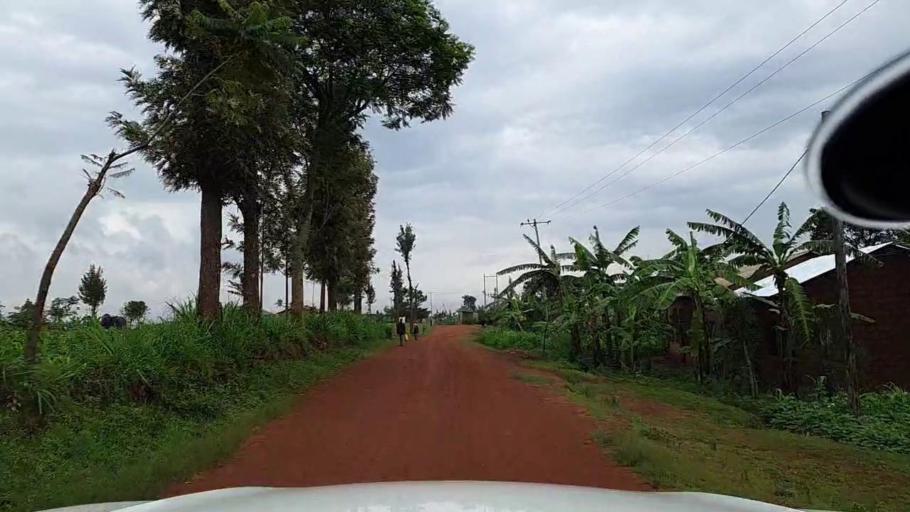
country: RW
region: Kigali
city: Kigali
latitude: -1.9284
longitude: 29.9001
